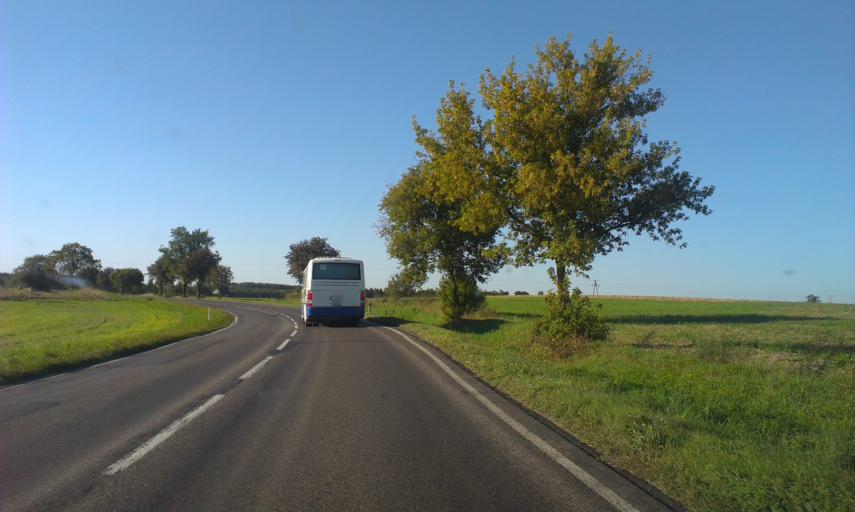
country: PL
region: Kujawsko-Pomorskie
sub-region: Powiat tucholski
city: Lubiewo
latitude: 53.5105
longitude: 17.9750
